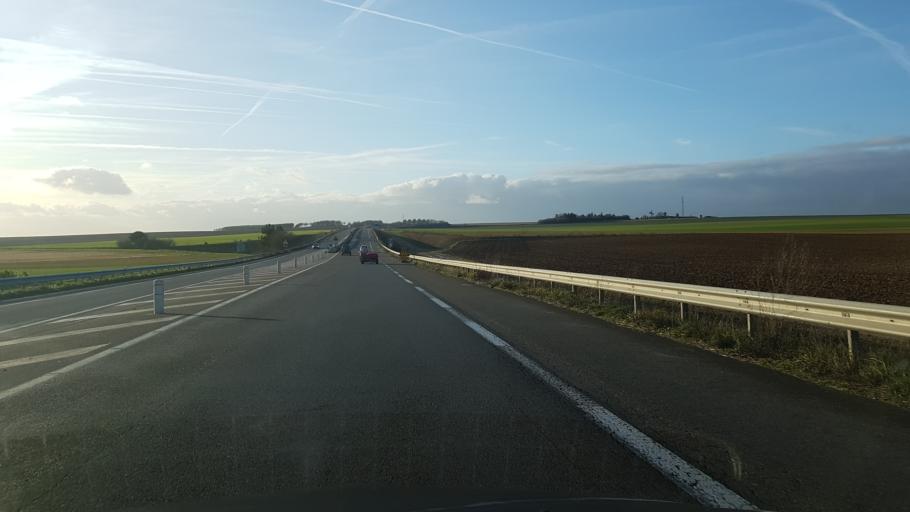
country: FR
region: Champagne-Ardenne
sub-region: Departement de l'Aube
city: Mailly-le-Camp
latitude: 48.7323
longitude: 4.2554
